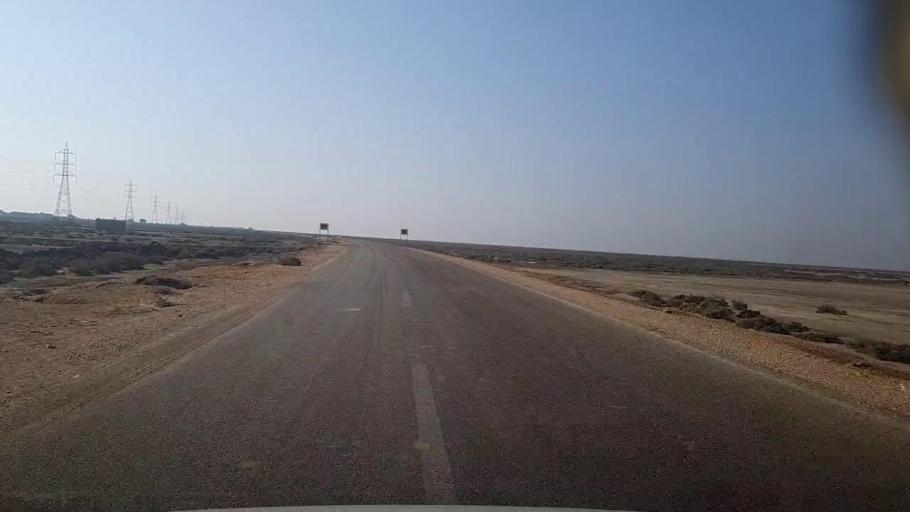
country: PK
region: Sindh
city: Gharo
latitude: 24.6291
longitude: 67.4972
